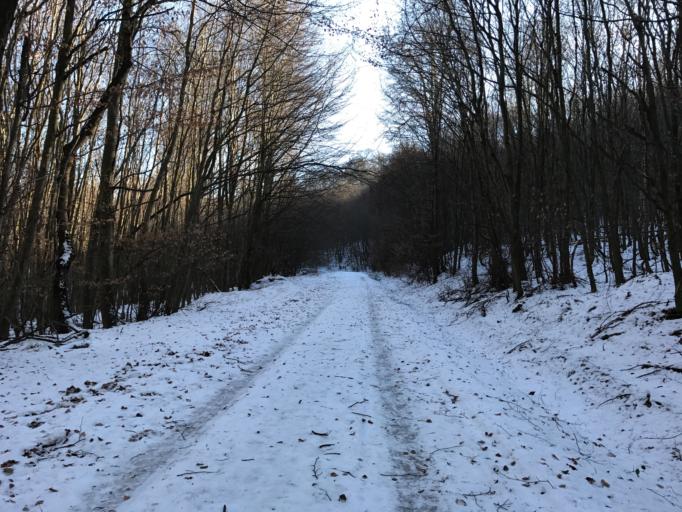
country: DE
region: Hesse
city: Eppstein
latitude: 50.1329
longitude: 8.3869
